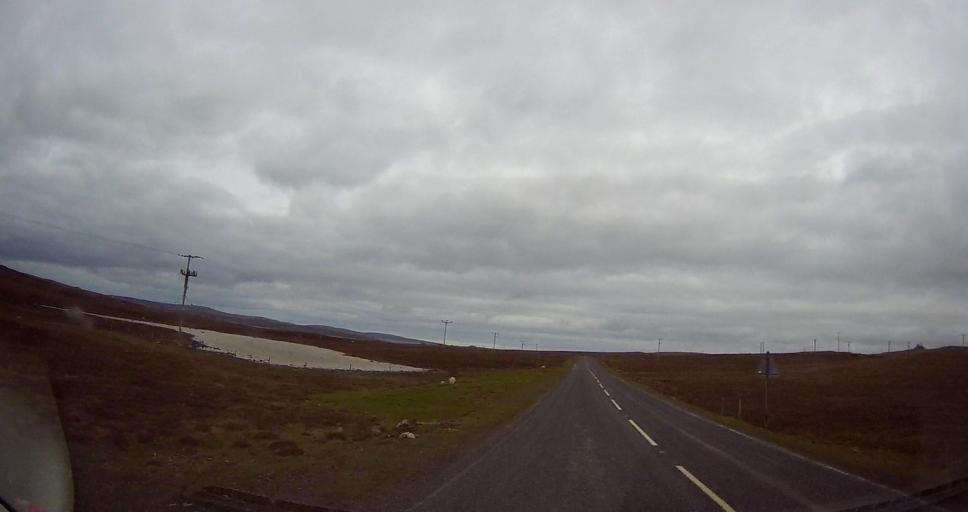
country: GB
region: Scotland
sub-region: Shetland Islands
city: Shetland
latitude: 60.7135
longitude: -0.9157
